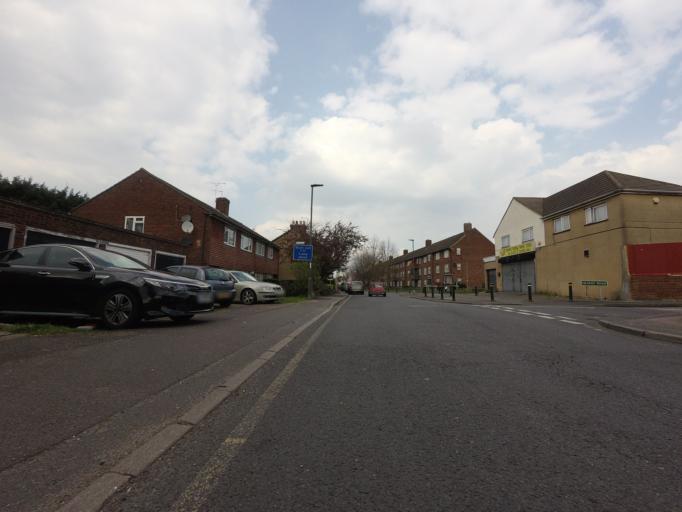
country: GB
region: England
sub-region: Greater London
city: Orpington
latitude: 51.3963
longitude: 0.1153
